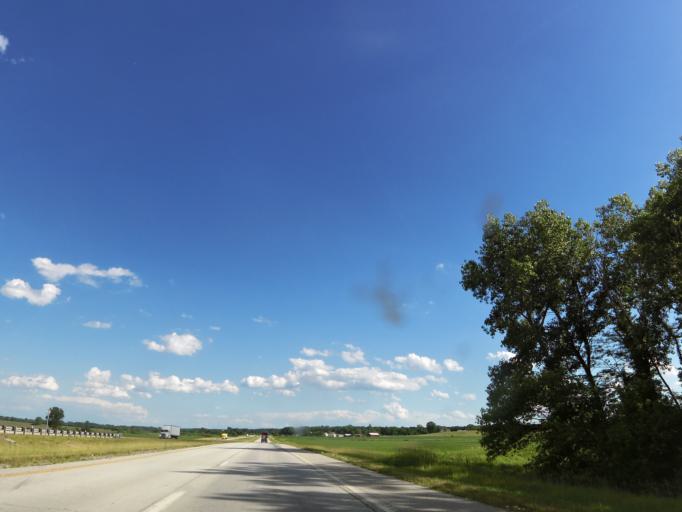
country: US
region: Illinois
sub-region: Hancock County
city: Warsaw
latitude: 40.2983
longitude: -91.5716
